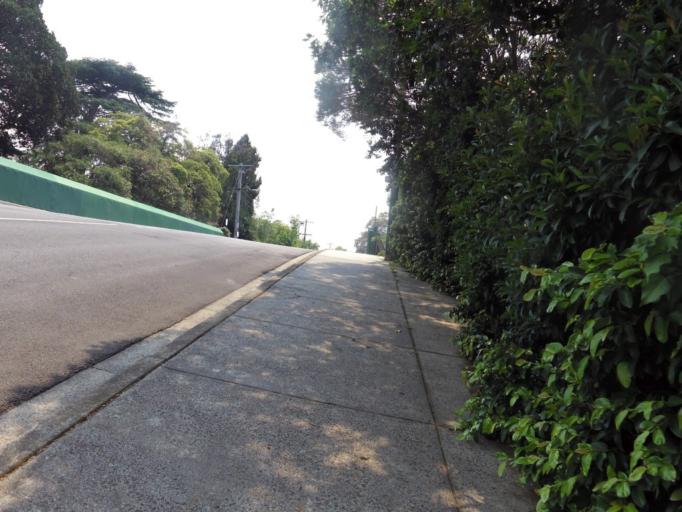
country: AU
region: Victoria
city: Toorak
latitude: -37.8243
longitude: 145.0203
